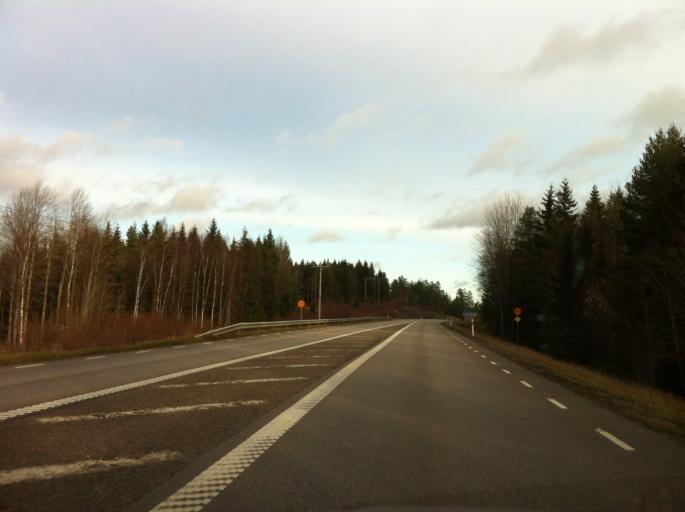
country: SE
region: Kronoberg
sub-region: Uppvidinge Kommun
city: Aseda
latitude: 57.1313
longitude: 15.2738
